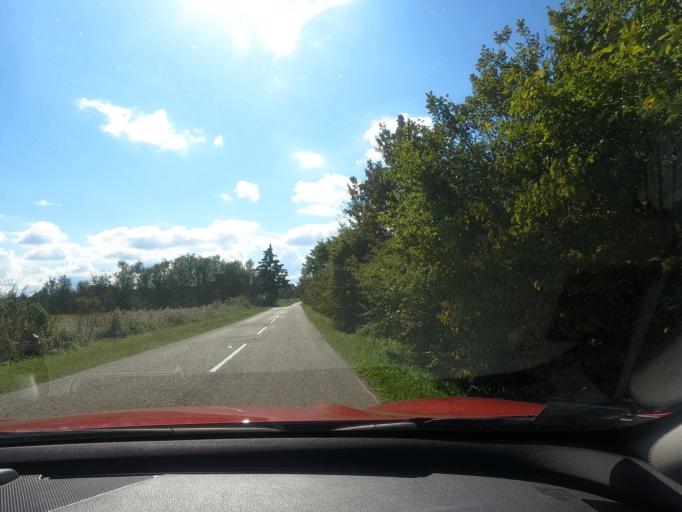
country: BA
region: Federation of Bosnia and Herzegovina
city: Vrnograc
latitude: 45.2451
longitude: 15.9433
